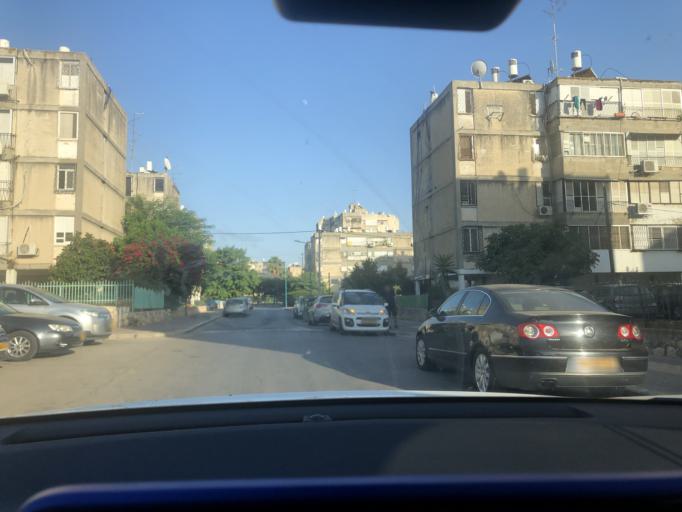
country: IL
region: Central District
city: Lod
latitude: 31.9522
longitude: 34.8890
